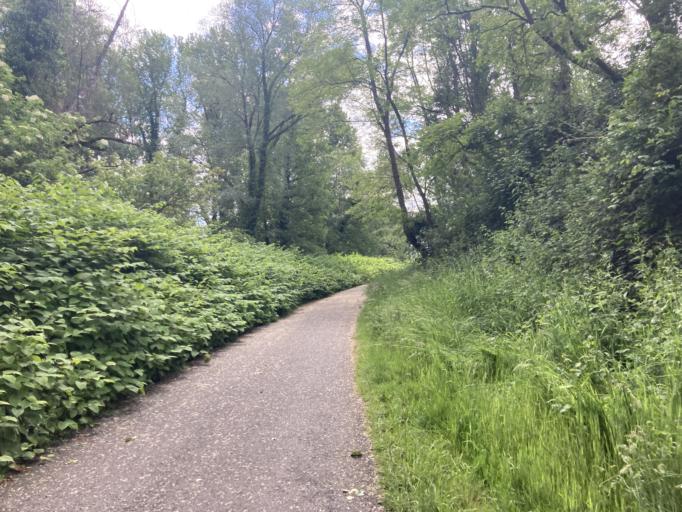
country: FR
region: Aquitaine
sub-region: Departement des Pyrenees-Atlantiques
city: Artiguelouve
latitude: 43.3247
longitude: -0.4578
